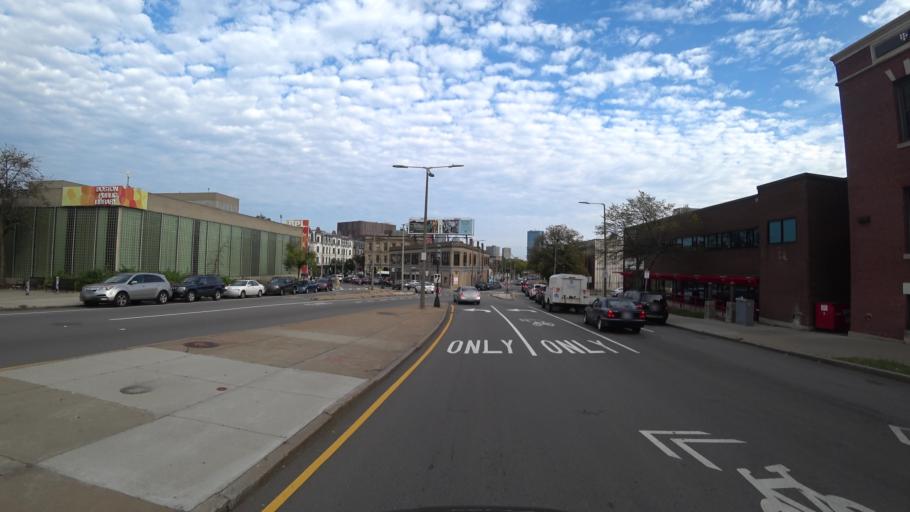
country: US
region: Massachusetts
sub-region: Suffolk County
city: South Boston
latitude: 42.3276
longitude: -71.0831
